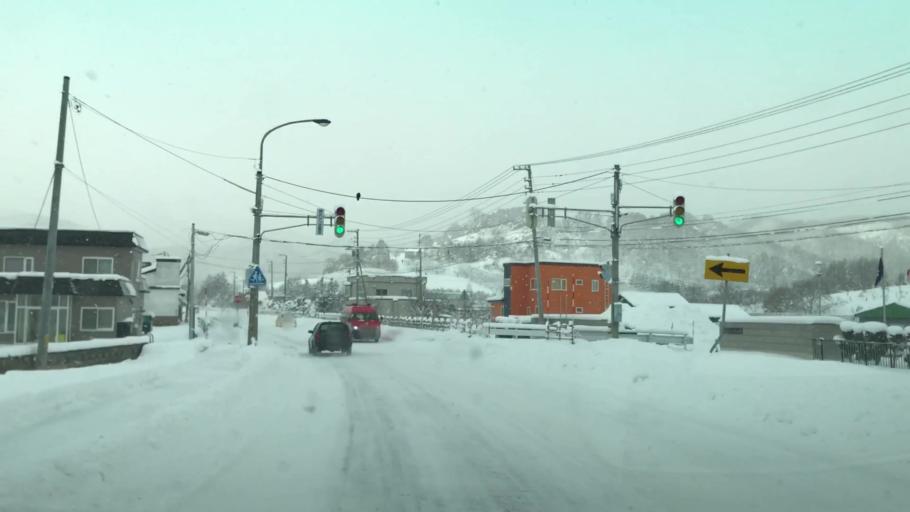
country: JP
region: Hokkaido
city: Yoichi
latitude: 43.2096
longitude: 140.7641
